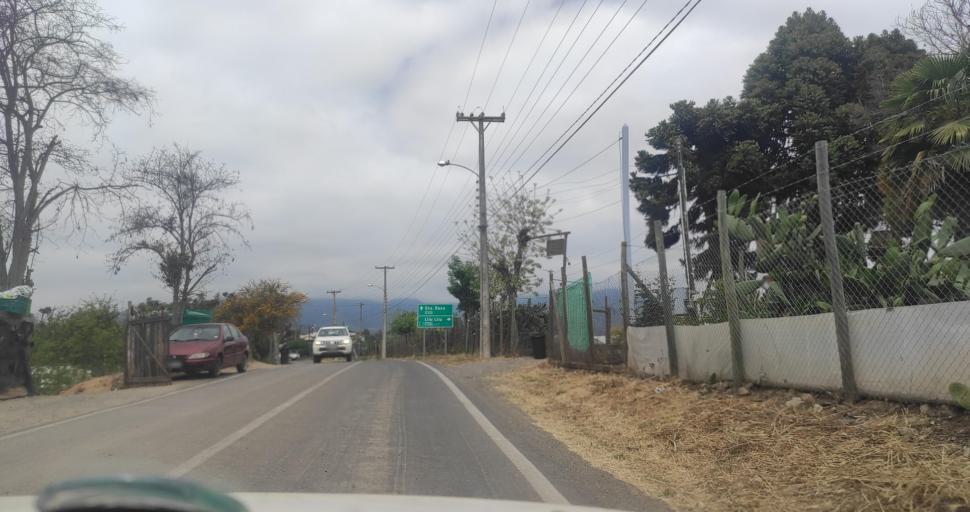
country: CL
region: Valparaiso
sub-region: Provincia de Marga Marga
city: Limache
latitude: -33.0218
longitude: -71.2280
